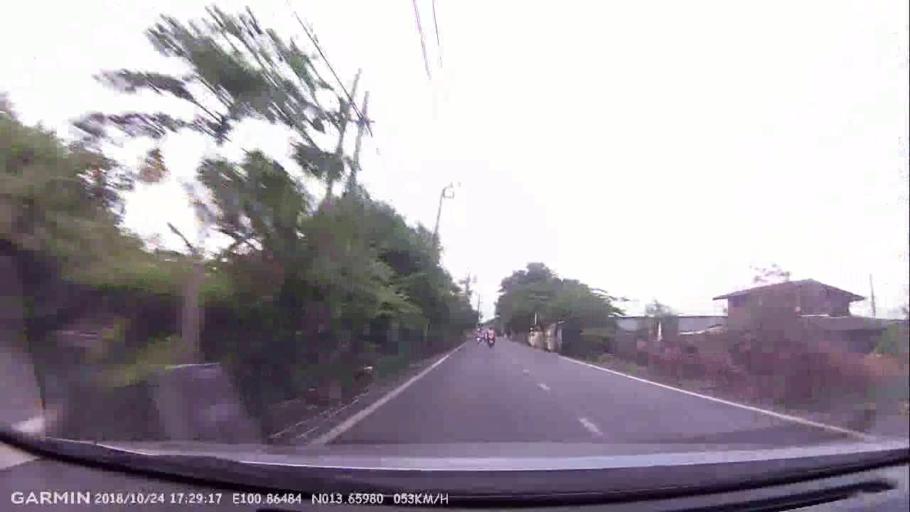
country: TH
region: Samut Prakan
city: Ban Khlong Bang Sao Thong
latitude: 13.6599
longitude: 100.8649
